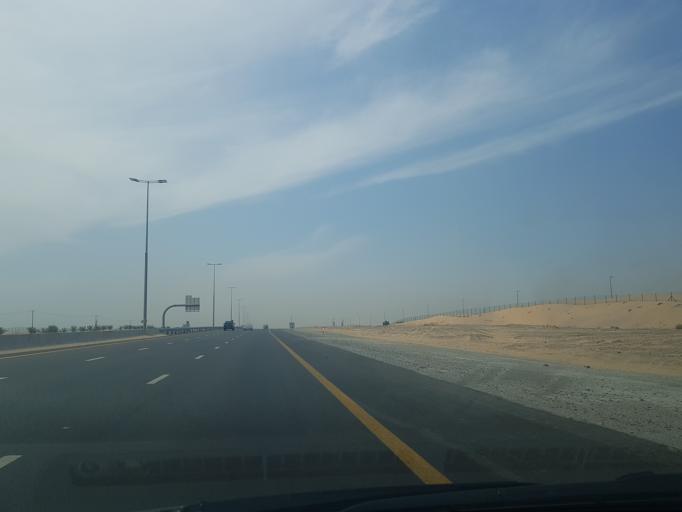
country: AE
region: Ash Shariqah
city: Sharjah
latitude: 25.2275
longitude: 55.5950
